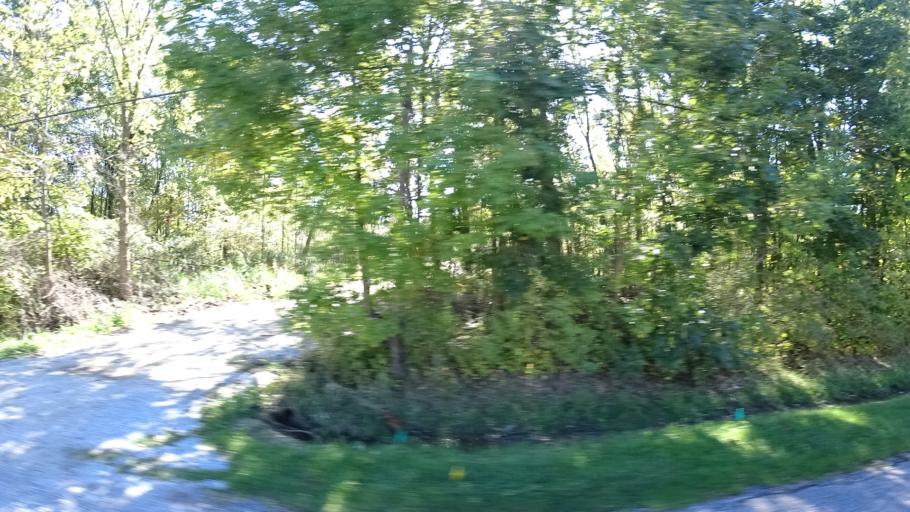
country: US
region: Indiana
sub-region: LaPorte County
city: Trail Creek
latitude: 41.6803
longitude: -86.8789
